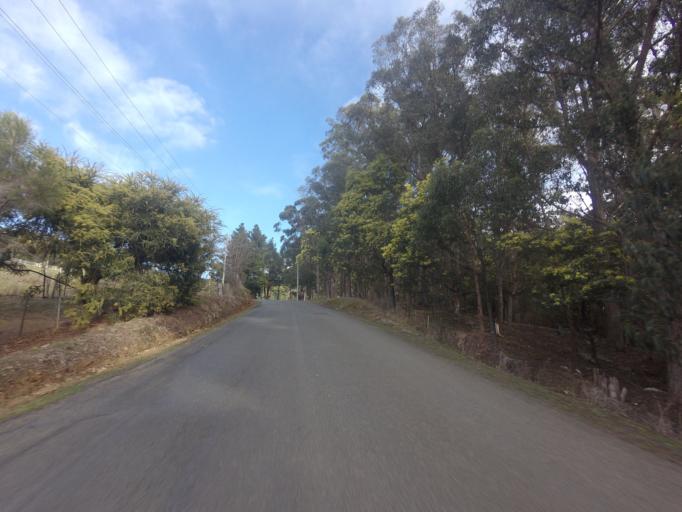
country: AU
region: Tasmania
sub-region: Kingborough
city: Margate
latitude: -42.9975
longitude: 147.1790
